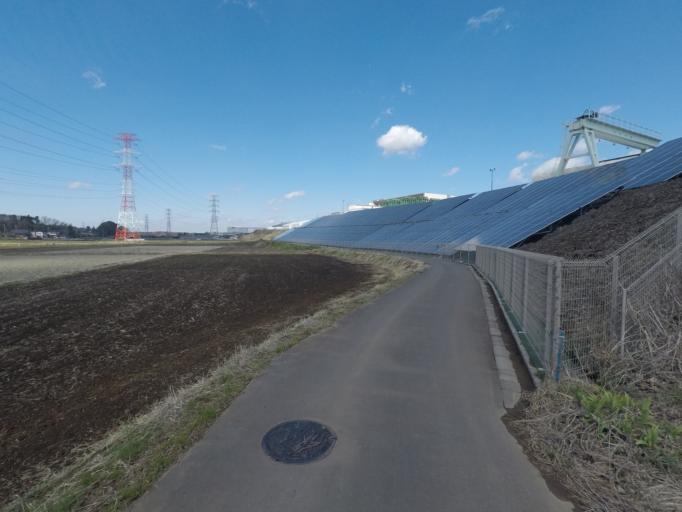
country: JP
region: Ibaraki
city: Ushiku
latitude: 36.0085
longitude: 140.0687
